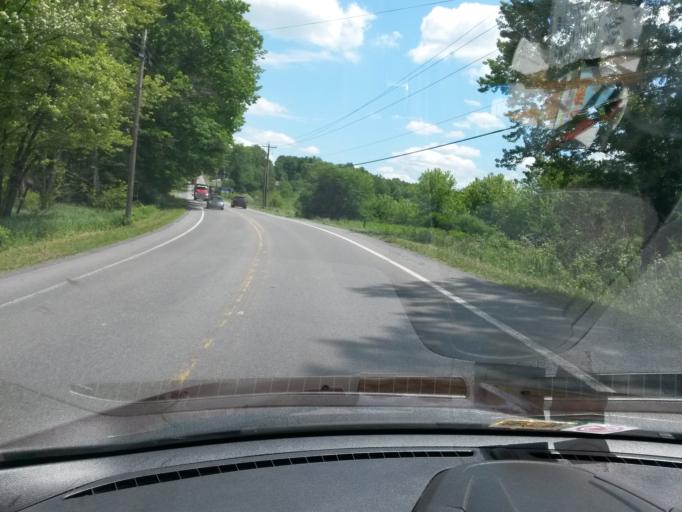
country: US
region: West Virginia
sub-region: Greenbrier County
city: Rainelle
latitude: 37.9565
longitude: -80.6823
